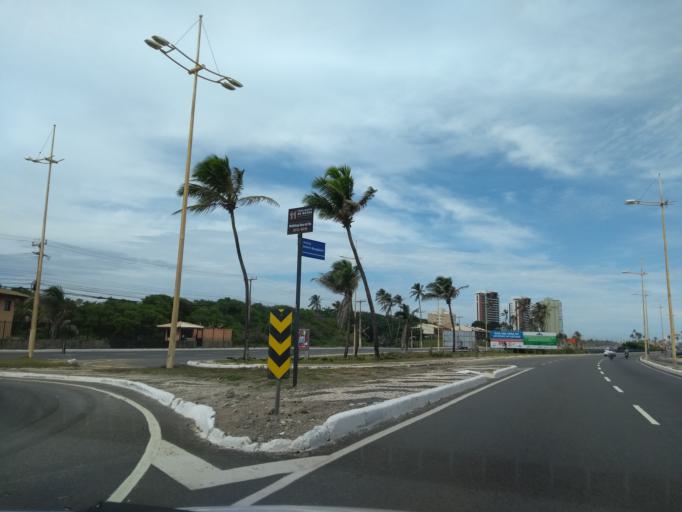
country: BR
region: Bahia
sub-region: Lauro De Freitas
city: Lauro de Freitas
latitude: -12.9626
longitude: -38.4003
